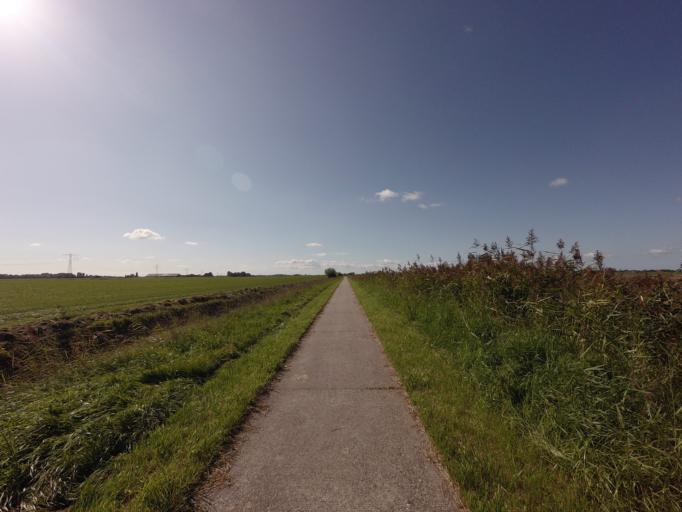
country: NL
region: Friesland
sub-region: Gemeente Boarnsterhim
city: Reduzum
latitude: 53.1424
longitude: 5.7641
